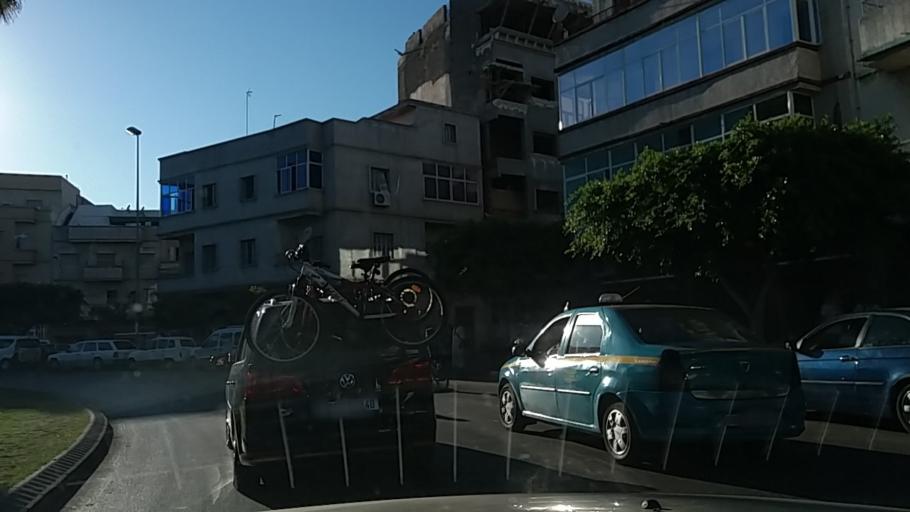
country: MA
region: Tanger-Tetouan
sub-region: Tanger-Assilah
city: Tangier
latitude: 35.7705
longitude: -5.8216
